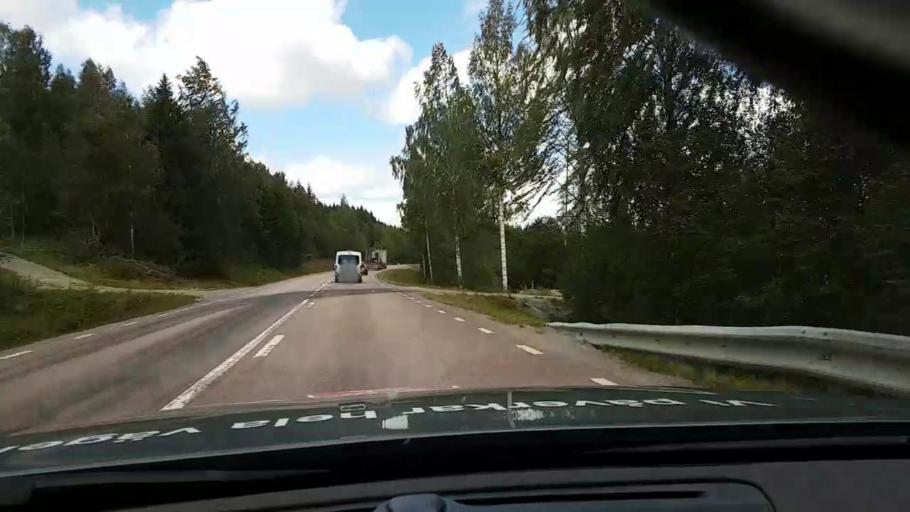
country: SE
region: Vaesternorrland
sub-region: OErnskoeldsviks Kommun
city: Bjasta
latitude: 63.3630
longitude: 18.4581
